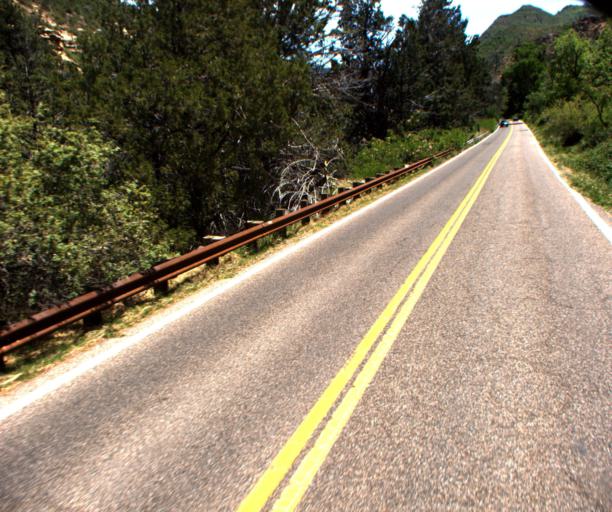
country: US
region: Arizona
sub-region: Coconino County
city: Sedona
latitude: 34.9429
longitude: -111.7522
